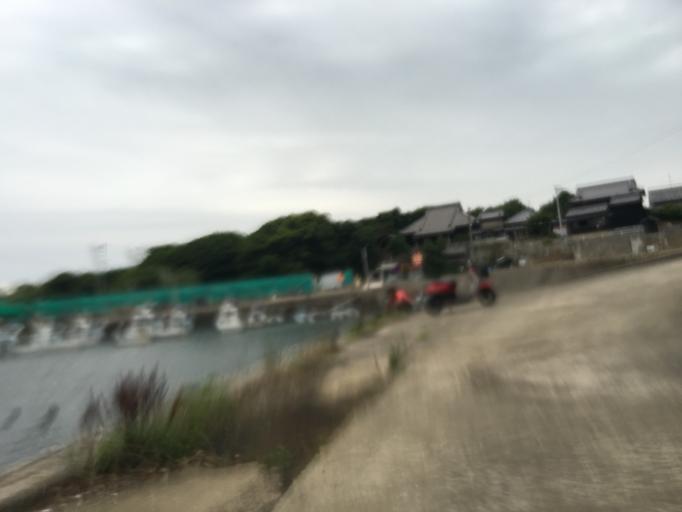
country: JP
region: Aichi
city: Ishiki
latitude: 34.7255
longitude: 137.0337
